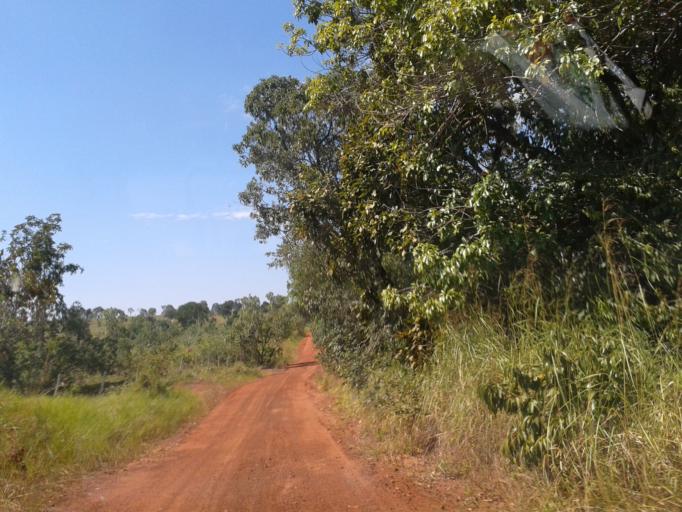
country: BR
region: Minas Gerais
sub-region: Campina Verde
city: Campina Verde
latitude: -19.4016
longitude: -49.7624
